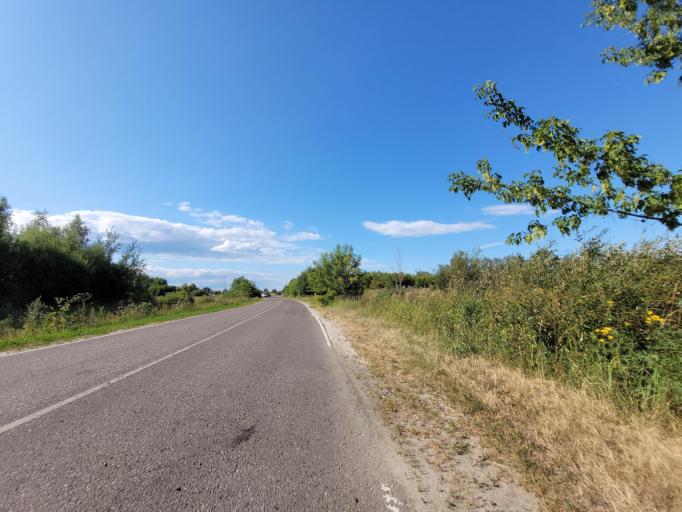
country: RU
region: Moskovskaya
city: Konobeyevo
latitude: 55.4031
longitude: 38.7082
